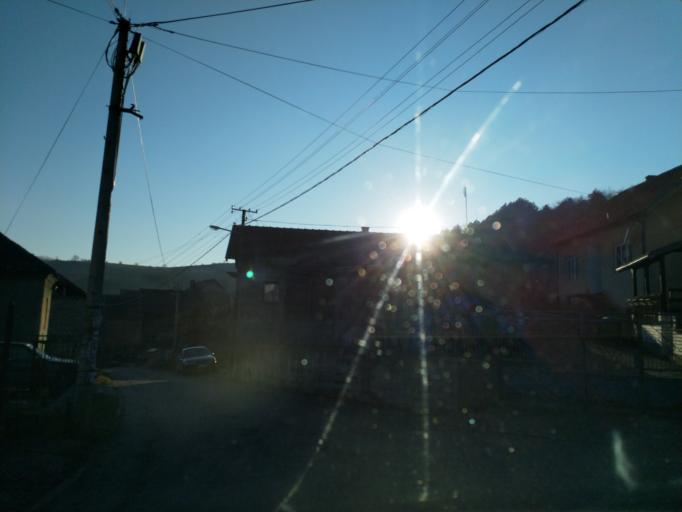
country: RS
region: Central Serbia
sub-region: Pomoravski Okrug
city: Paracin
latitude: 43.9362
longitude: 21.5215
